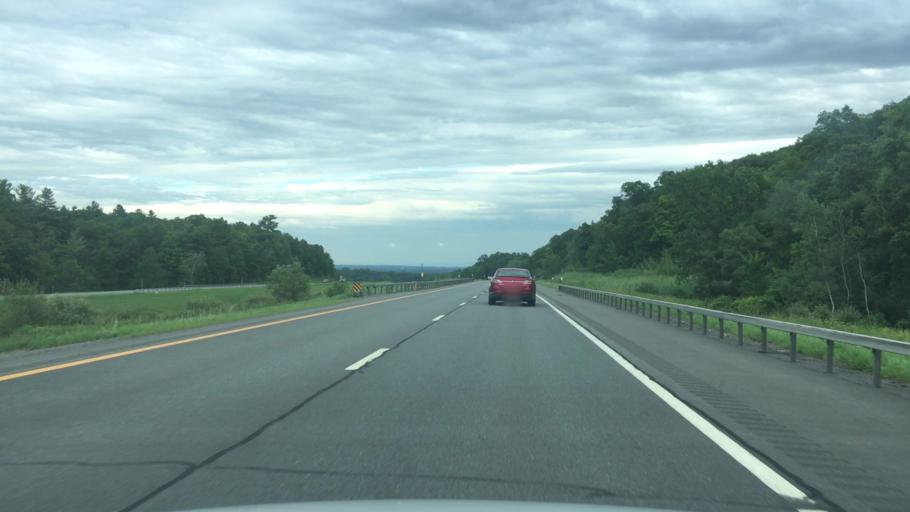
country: US
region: New York
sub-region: Albany County
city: Altamont
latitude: 42.7715
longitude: -74.0716
